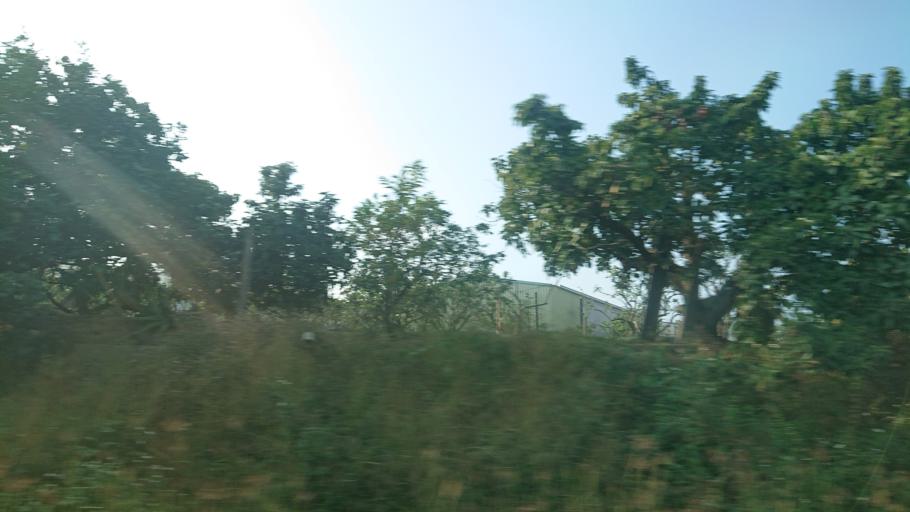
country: TW
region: Taiwan
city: Xinying
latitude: 23.1684
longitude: 120.2542
